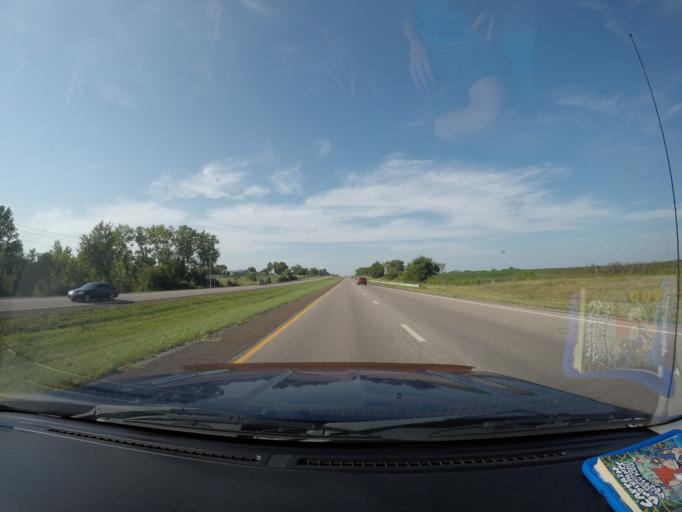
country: US
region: Kansas
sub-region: Leavenworth County
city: Basehor
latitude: 39.1731
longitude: -94.9004
